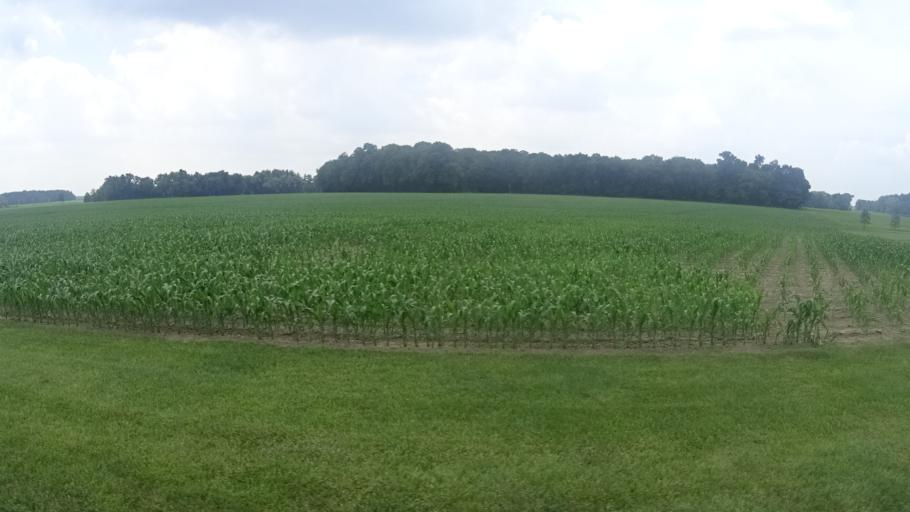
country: US
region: Ohio
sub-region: Erie County
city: Milan
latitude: 41.3147
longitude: -82.6697
